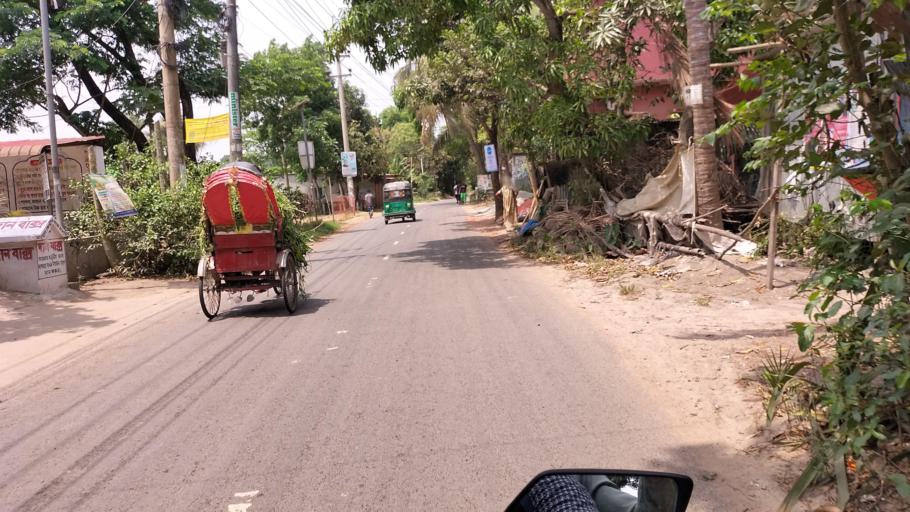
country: BD
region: Dhaka
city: Azimpur
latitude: 23.7310
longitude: 90.3075
